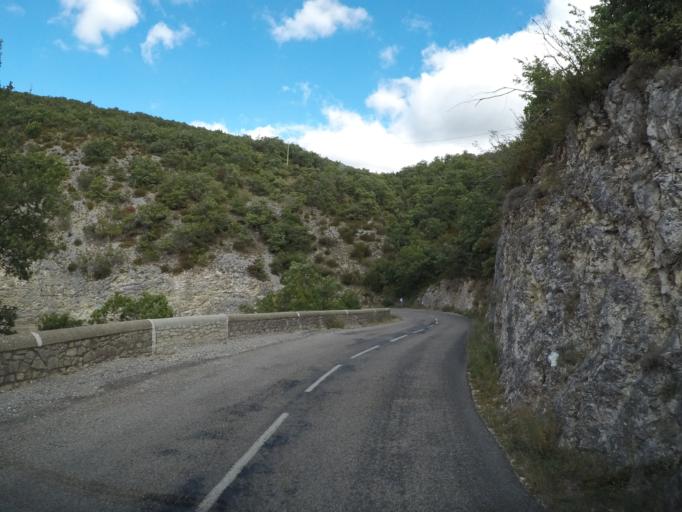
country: FR
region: Provence-Alpes-Cote d'Azur
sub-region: Departement du Vaucluse
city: Sault
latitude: 44.1554
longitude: 5.4471
